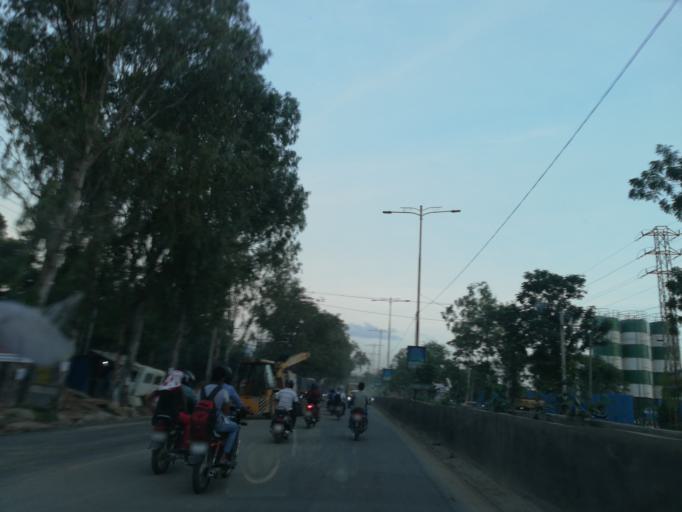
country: IN
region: Telangana
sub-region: Medak
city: Serilingampalle
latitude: 17.5243
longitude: 78.3556
